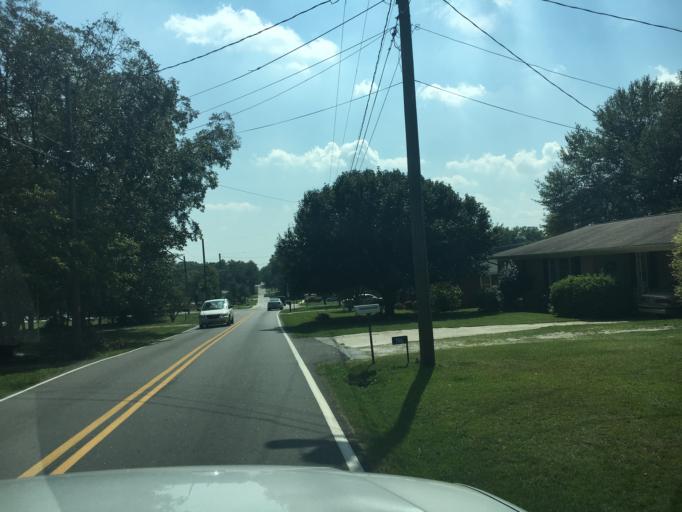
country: US
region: Georgia
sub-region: Hart County
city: Hartwell
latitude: 34.3513
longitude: -82.9192
